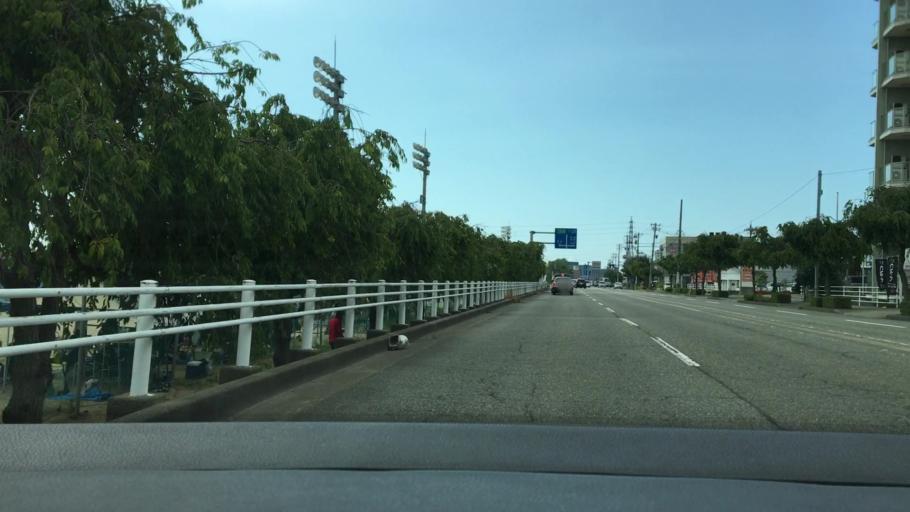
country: JP
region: Ishikawa
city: Kanazawa-shi
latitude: 36.5721
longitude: 136.6326
